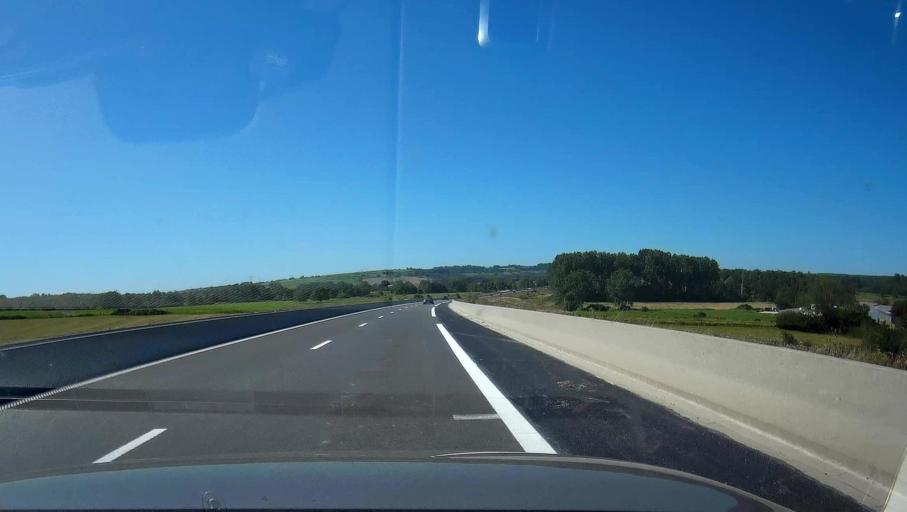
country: FR
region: Champagne-Ardenne
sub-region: Departement des Ardennes
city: Rimogne
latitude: 49.7917
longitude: 4.5465
